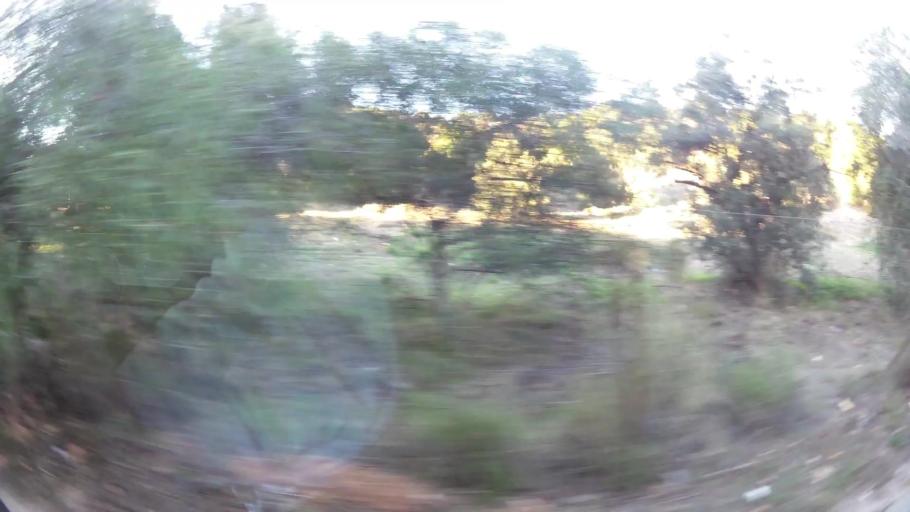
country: GR
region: Attica
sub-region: Nomarchia Anatolikis Attikis
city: Vouliagmeni
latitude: 37.8233
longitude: 23.7892
